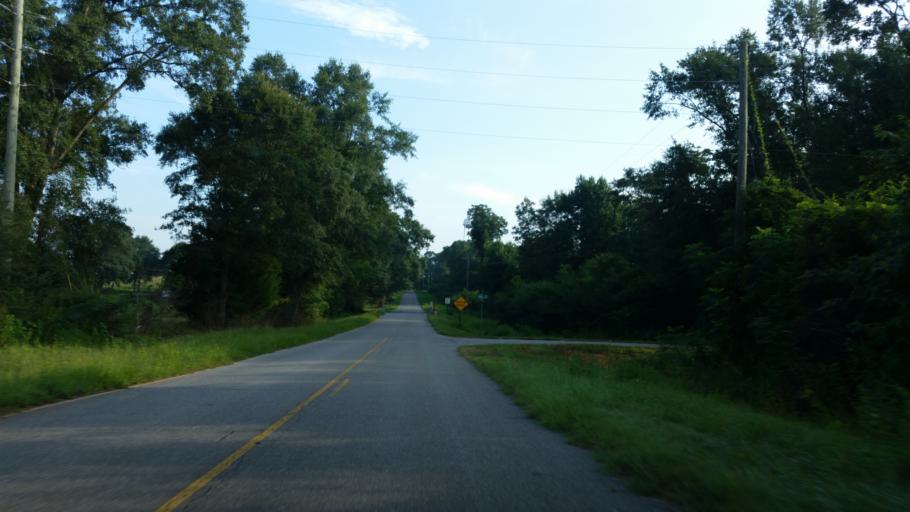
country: US
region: Alabama
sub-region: Escambia County
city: Atmore
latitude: 30.9867
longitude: -87.5713
